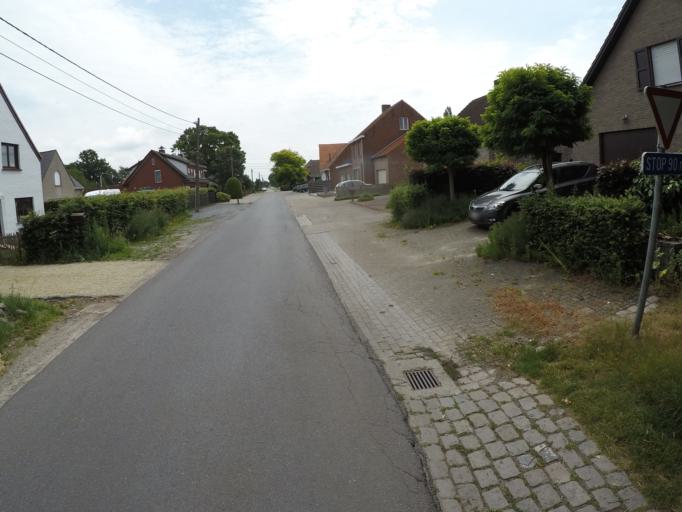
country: BE
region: Flanders
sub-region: Provincie Antwerpen
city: Essen
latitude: 51.4362
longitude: 4.5228
